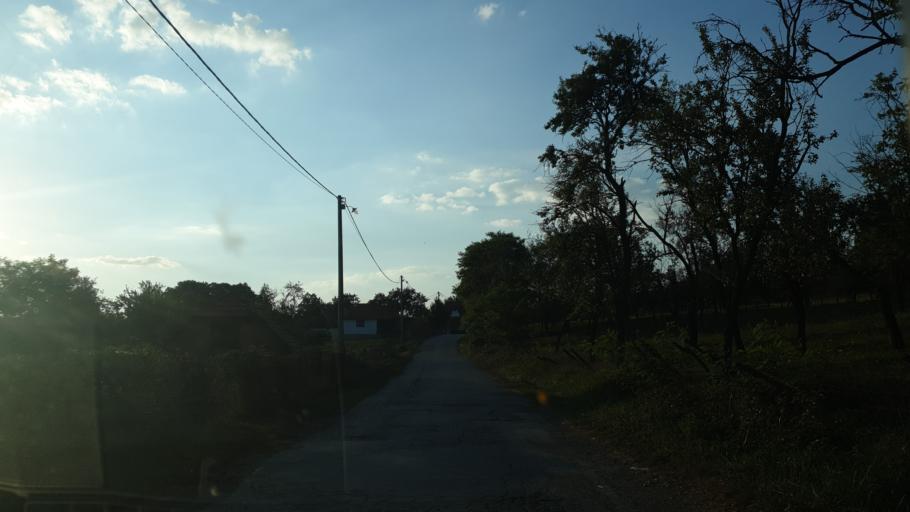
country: RS
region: Central Serbia
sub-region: Zlatiborski Okrug
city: Kosjeric
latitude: 43.9919
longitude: 20.0040
